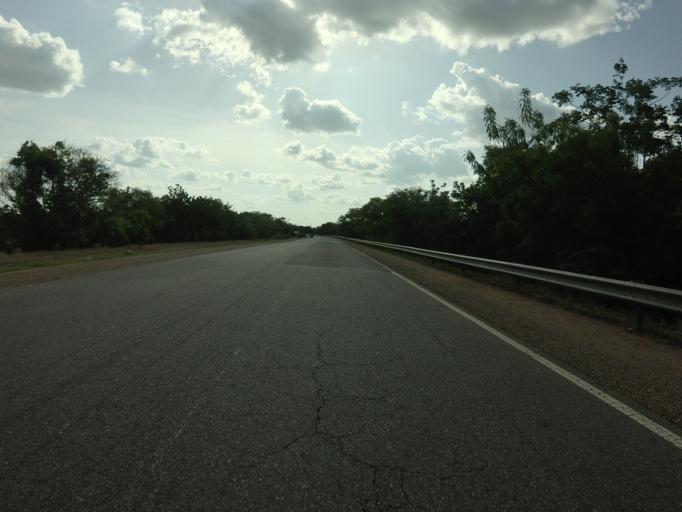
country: GH
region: Upper East
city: Bolgatanga
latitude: 10.5841
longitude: -0.8355
